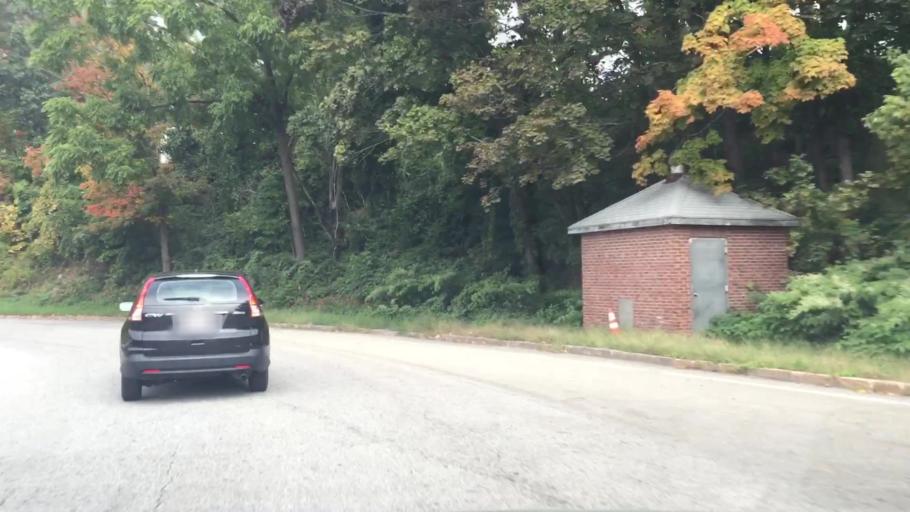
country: US
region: Massachusetts
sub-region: Middlesex County
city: Dracut
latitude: 42.6484
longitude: -71.2985
